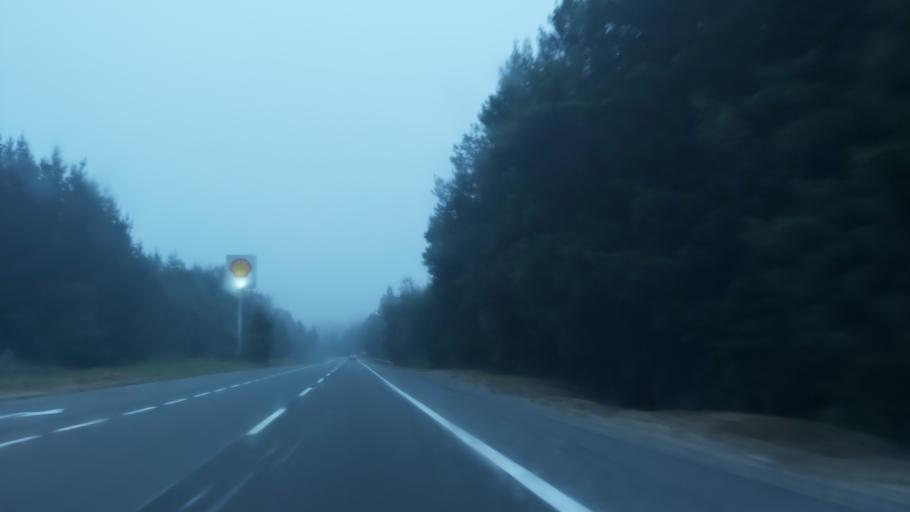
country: CL
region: Biobio
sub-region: Provincia de Concepcion
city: Penco
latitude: -36.7480
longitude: -72.9208
